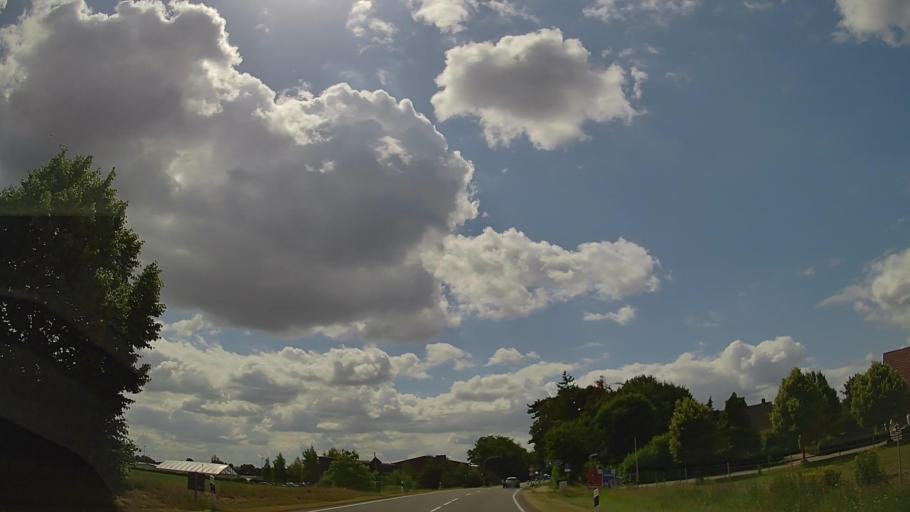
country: DE
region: Lower Saxony
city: Vechta
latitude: 52.7000
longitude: 8.3009
